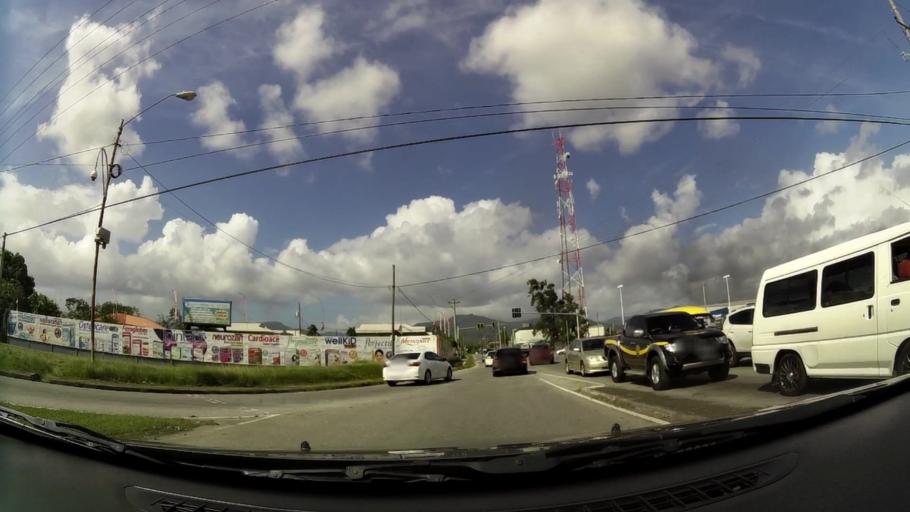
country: TT
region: Tunapuna/Piarco
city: Arouca
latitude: 10.6147
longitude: -61.3096
